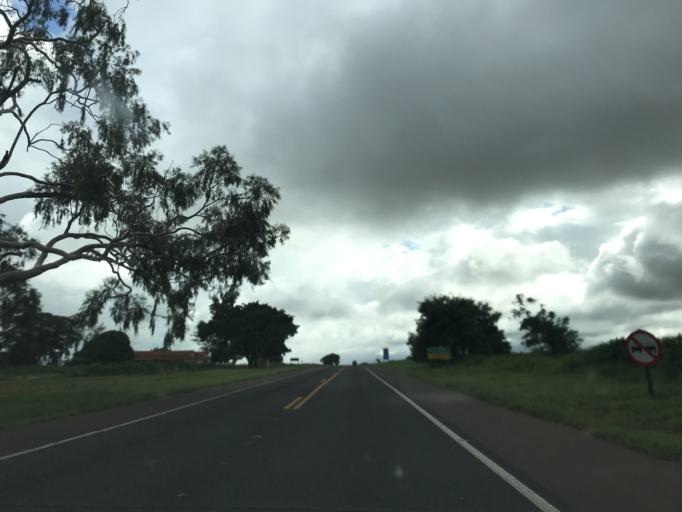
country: BR
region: Sao Paulo
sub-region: Penapolis
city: Penapolis
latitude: -21.4876
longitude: -50.2188
